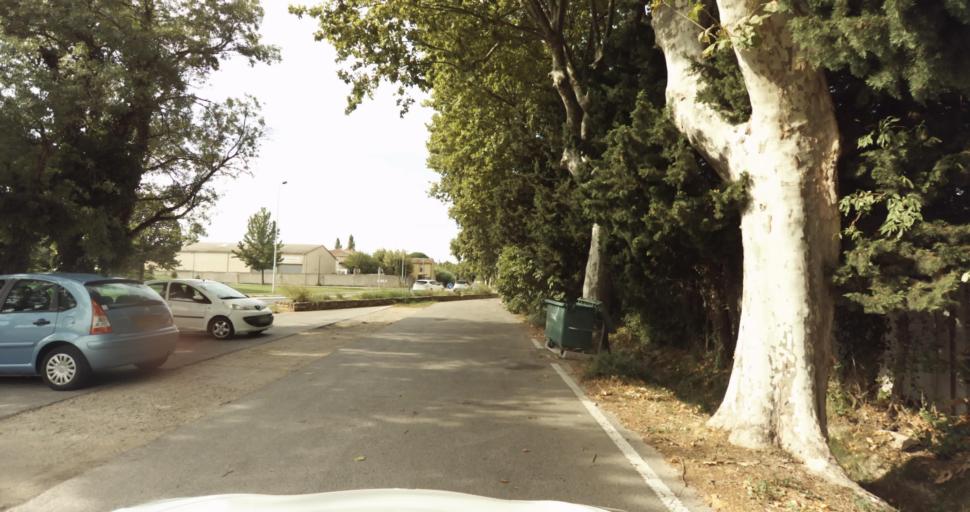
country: FR
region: Provence-Alpes-Cote d'Azur
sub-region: Departement des Bouches-du-Rhone
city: Miramas
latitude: 43.5717
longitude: 5.0193
